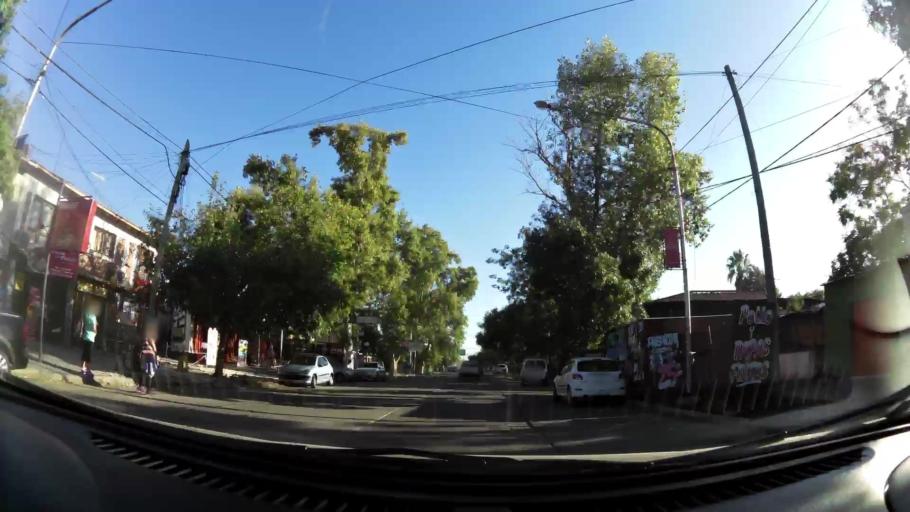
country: AR
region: Mendoza
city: Las Heras
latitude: -32.8640
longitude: -68.8220
